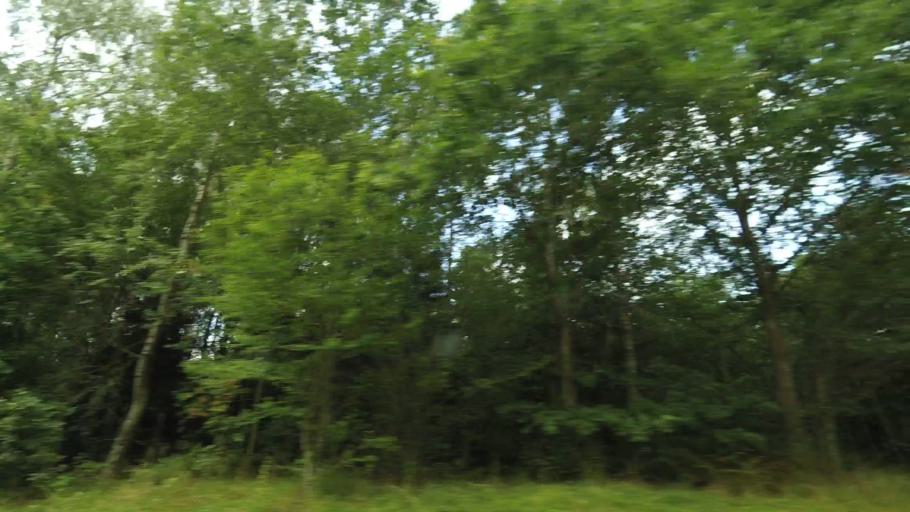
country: DK
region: Central Jutland
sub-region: Syddjurs Kommune
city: Ryomgard
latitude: 56.4187
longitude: 10.5587
